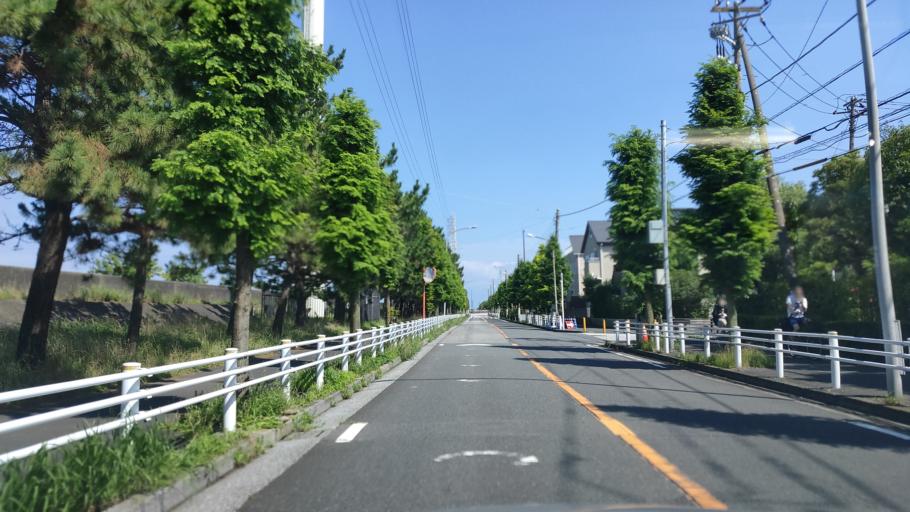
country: JP
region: Tokyo
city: Urayasu
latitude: 35.6535
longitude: 139.9207
